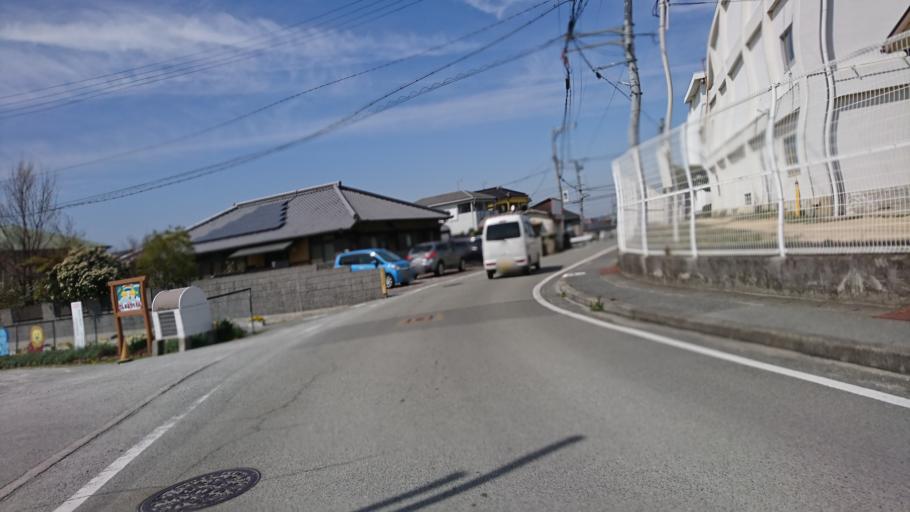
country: JP
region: Hyogo
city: Kakogawacho-honmachi
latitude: 34.7491
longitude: 134.9021
